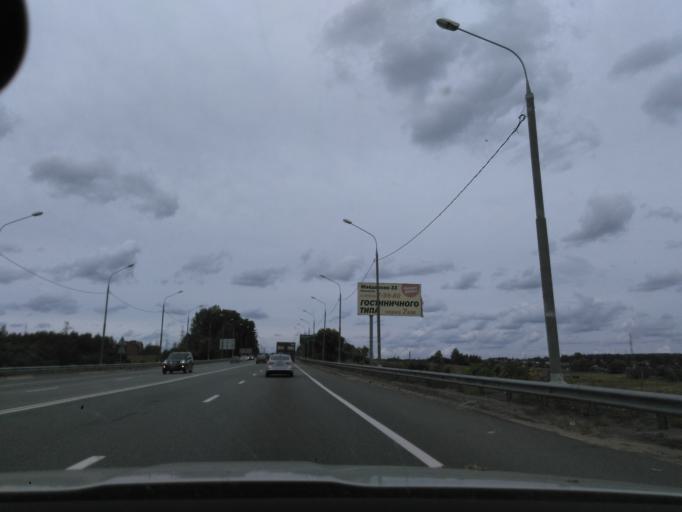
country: RU
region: Moskovskaya
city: Klin
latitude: 56.3016
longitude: 36.7930
